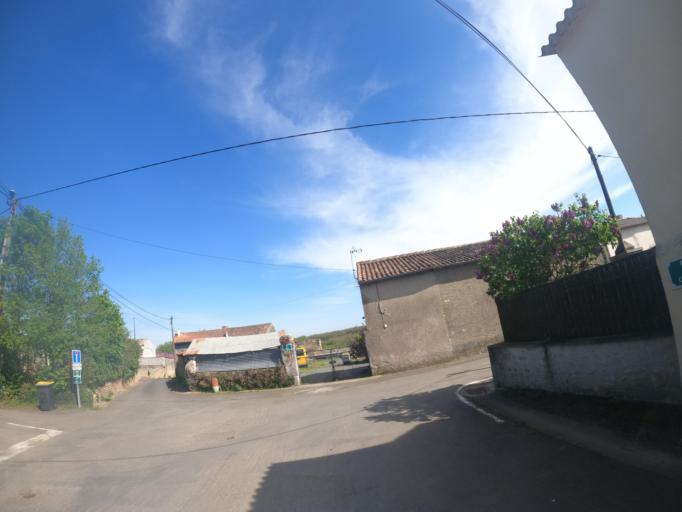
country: FR
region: Poitou-Charentes
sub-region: Departement des Deux-Sevres
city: Saint-Varent
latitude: 46.9118
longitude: -0.2128
